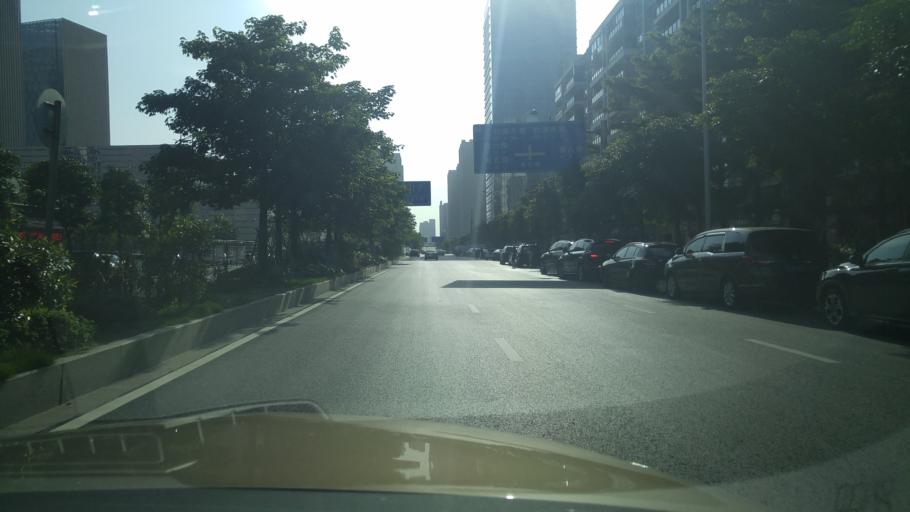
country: CN
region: Guangdong
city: Foshan
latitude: 23.0652
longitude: 113.1481
